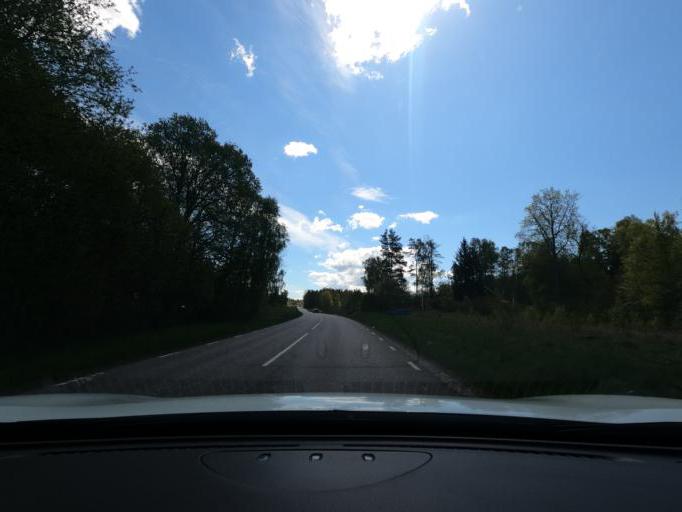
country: SE
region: Halland
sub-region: Kungsbacka Kommun
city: Fjaeras kyrkby
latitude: 57.4124
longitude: 12.2149
